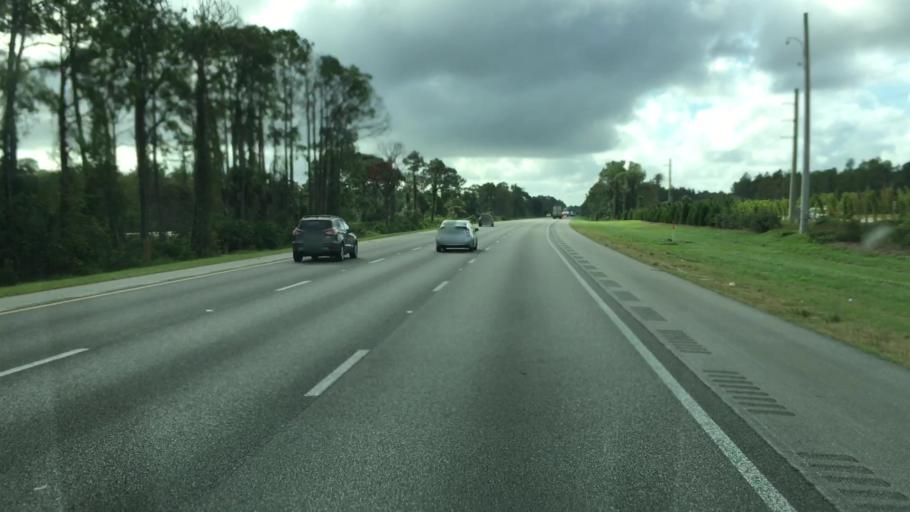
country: US
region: Florida
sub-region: Volusia County
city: Glencoe
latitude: 29.0618
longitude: -81.0086
